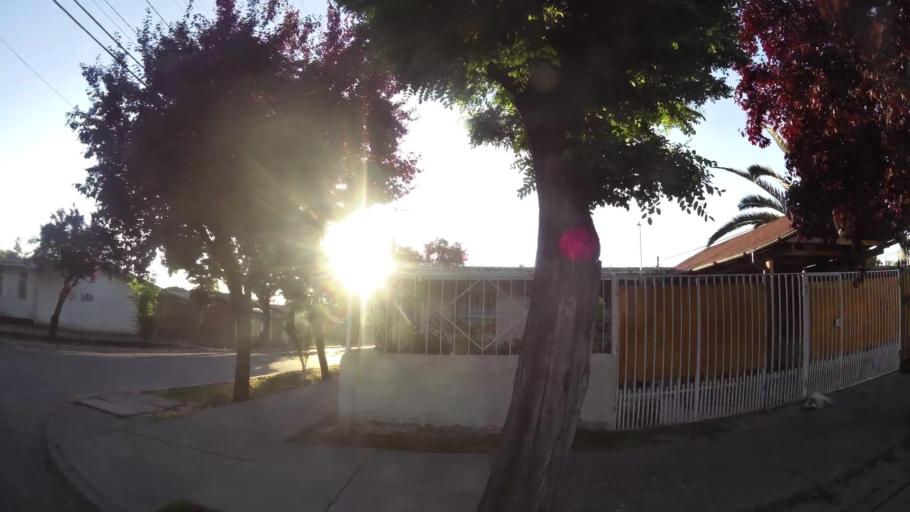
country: CL
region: Santiago Metropolitan
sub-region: Provincia de Maipo
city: San Bernardo
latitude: -33.5904
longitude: -70.6929
